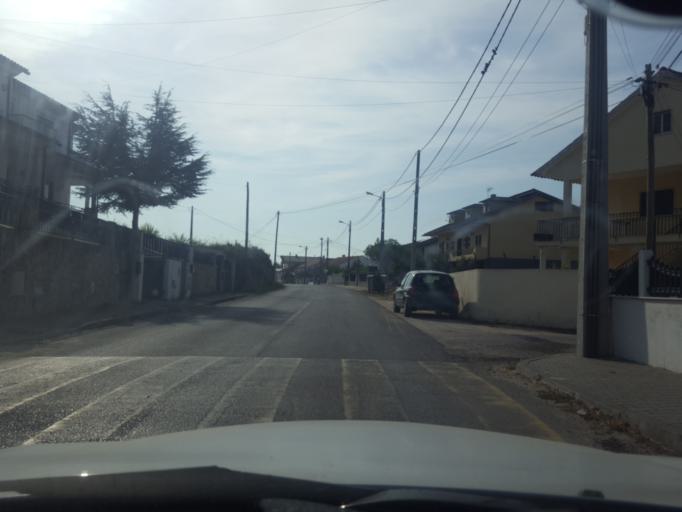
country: PT
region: Leiria
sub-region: Leiria
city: Leiria
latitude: 39.7252
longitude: -8.7729
